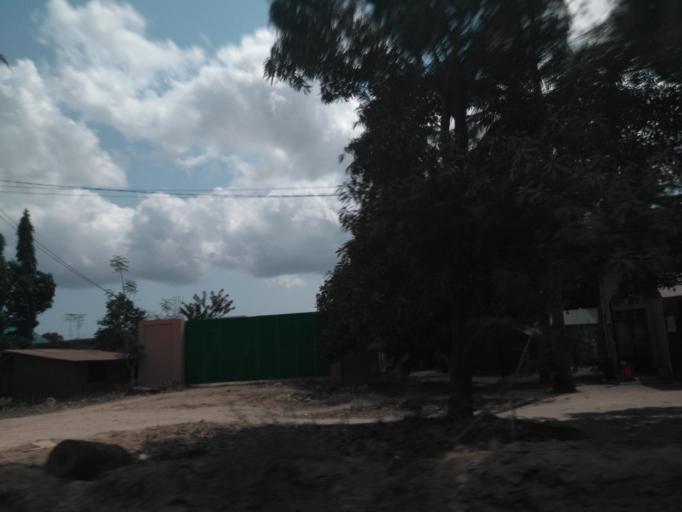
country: TZ
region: Dar es Salaam
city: Dar es Salaam
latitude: -6.8773
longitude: 39.3355
